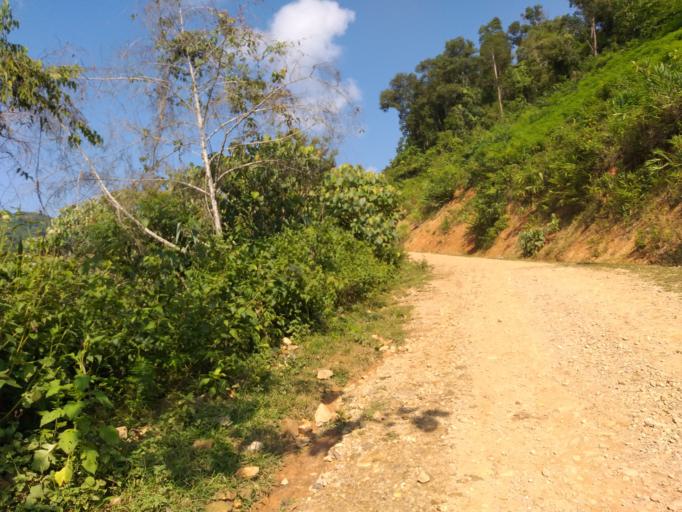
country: LA
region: Phongsali
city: Khoa
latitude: 21.2108
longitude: 102.6116
